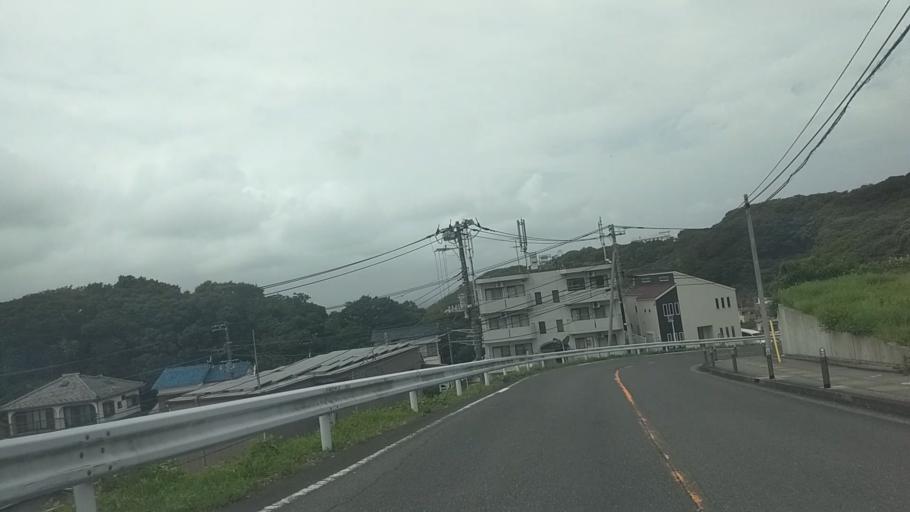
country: JP
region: Kanagawa
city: Yokosuka
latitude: 35.2555
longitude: 139.7190
